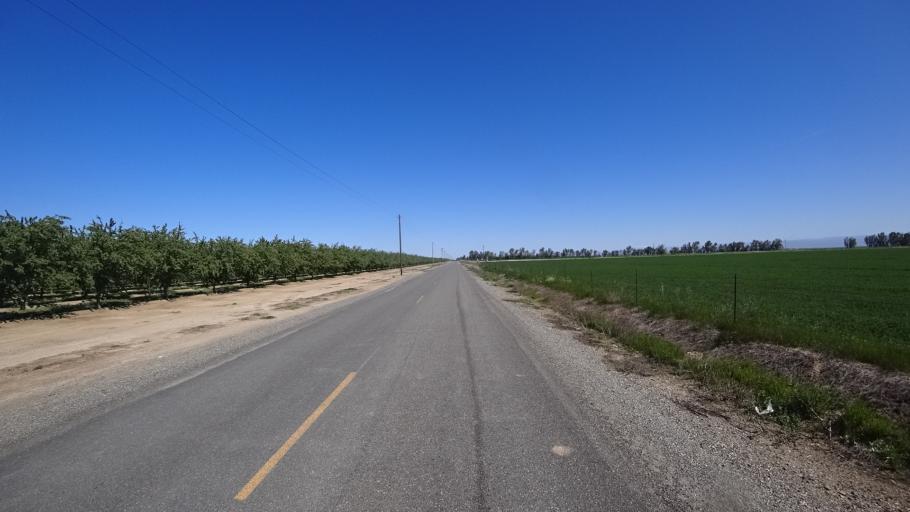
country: US
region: California
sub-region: Glenn County
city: Hamilton City
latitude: 39.6792
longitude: -122.1033
